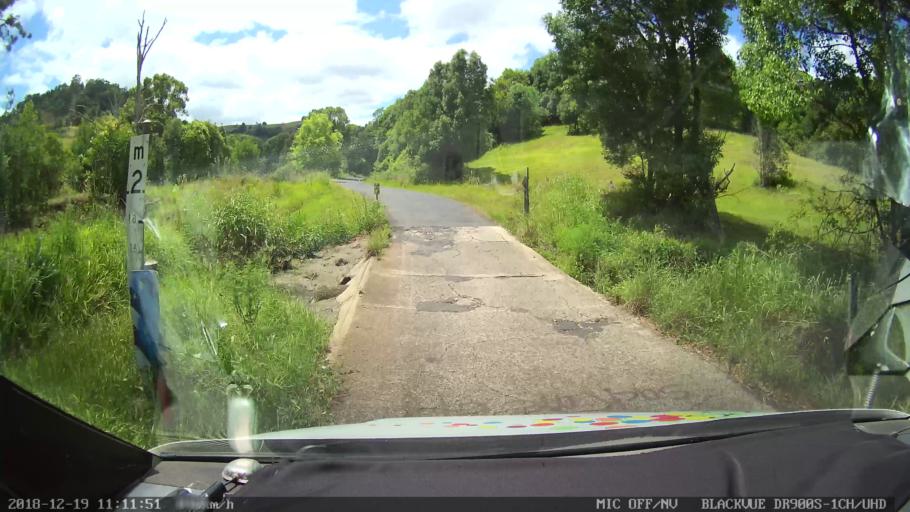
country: AU
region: New South Wales
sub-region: Lismore Municipality
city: Nimbin
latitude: -28.6457
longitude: 153.2590
